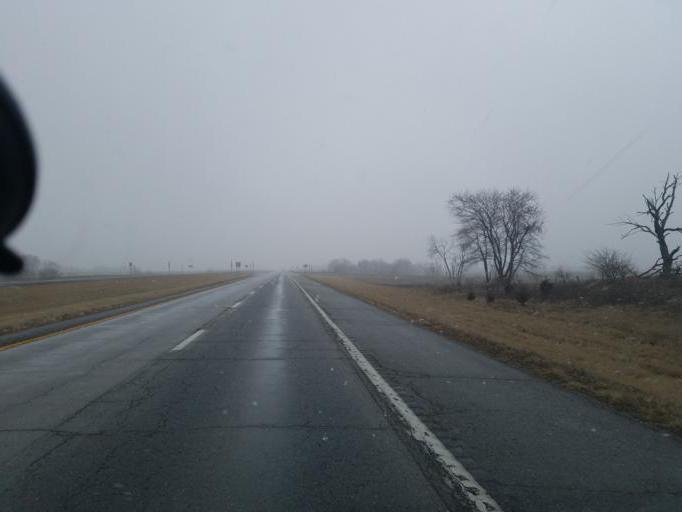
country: US
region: Missouri
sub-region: Macon County
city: La Plata
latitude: 39.9862
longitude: -92.4760
